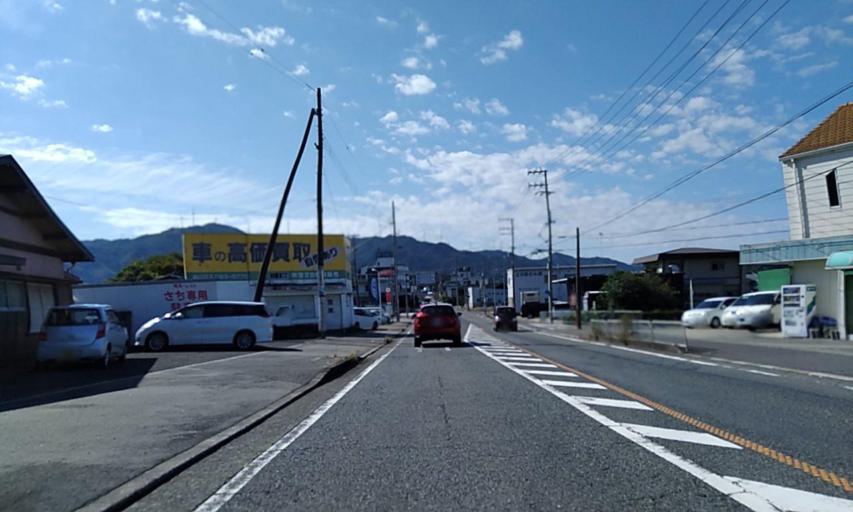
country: JP
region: Wakayama
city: Kainan
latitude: 34.0261
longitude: 135.1817
